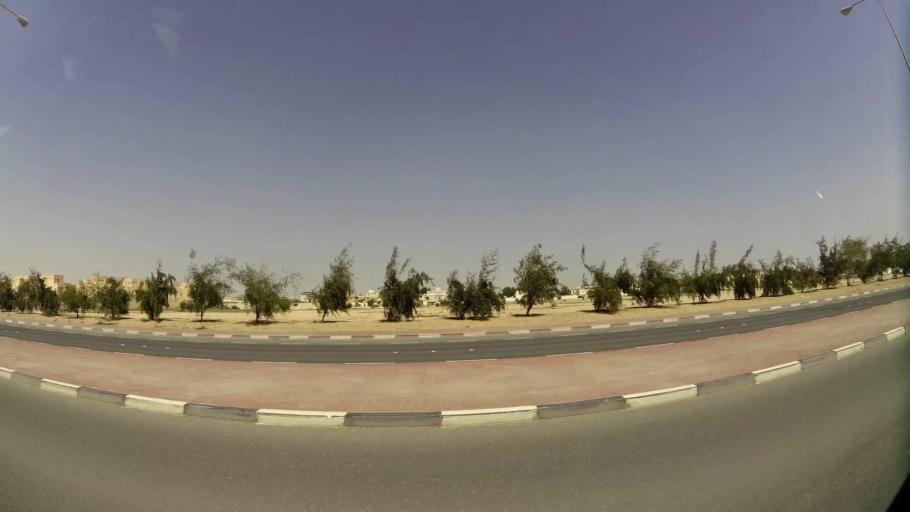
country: QA
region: Baladiyat Umm Salal
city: Umm Salal Muhammad
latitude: 25.3886
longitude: 51.4226
